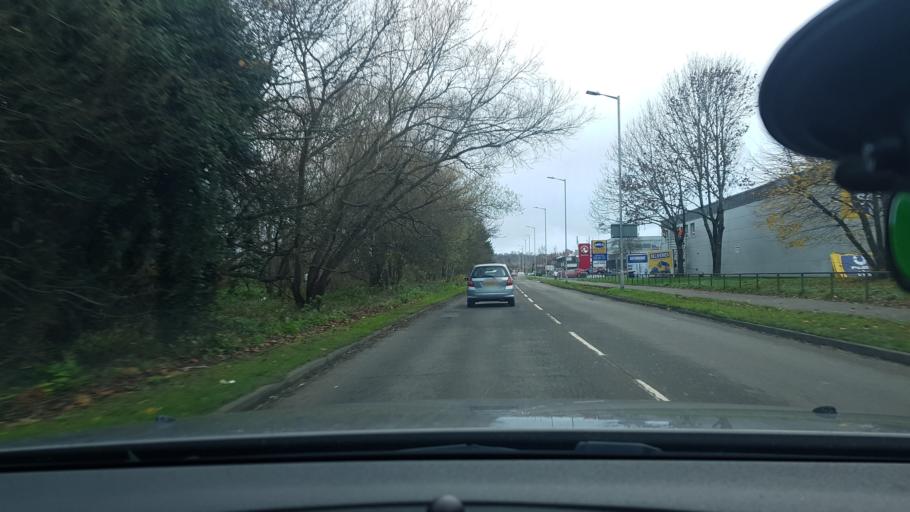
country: GB
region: England
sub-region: Reading
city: Reading
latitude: 51.4608
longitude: -0.9995
